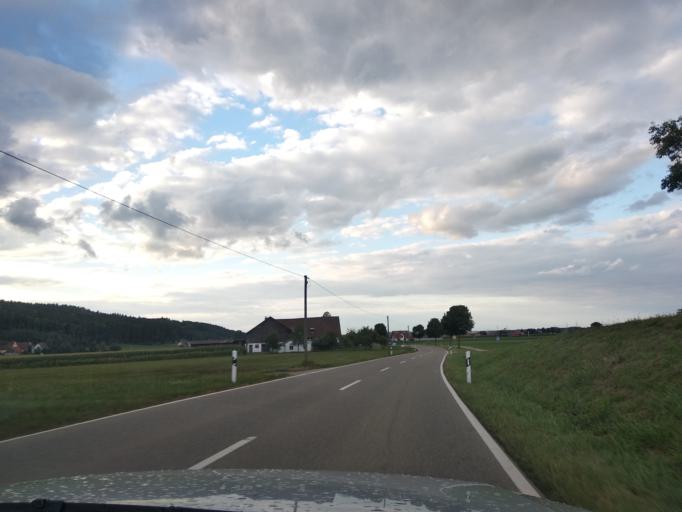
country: DE
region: Bavaria
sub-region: Swabia
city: Woringen
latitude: 47.9072
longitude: 10.2049
